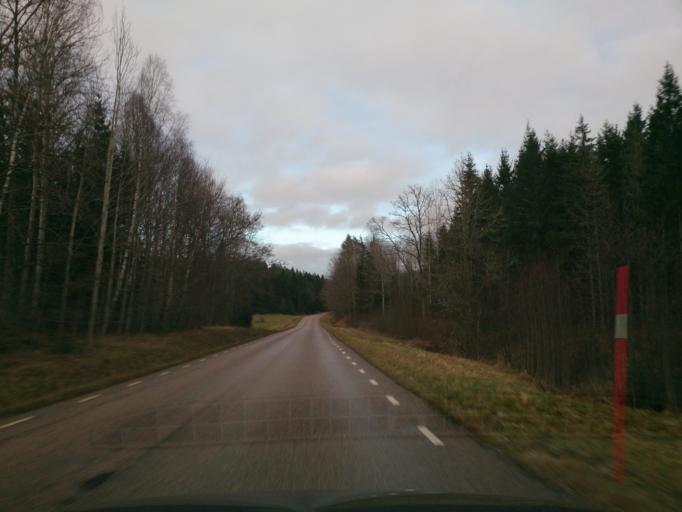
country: SE
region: OEstergoetland
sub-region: Atvidabergs Kommun
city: Atvidaberg
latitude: 58.2943
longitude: 16.0050
